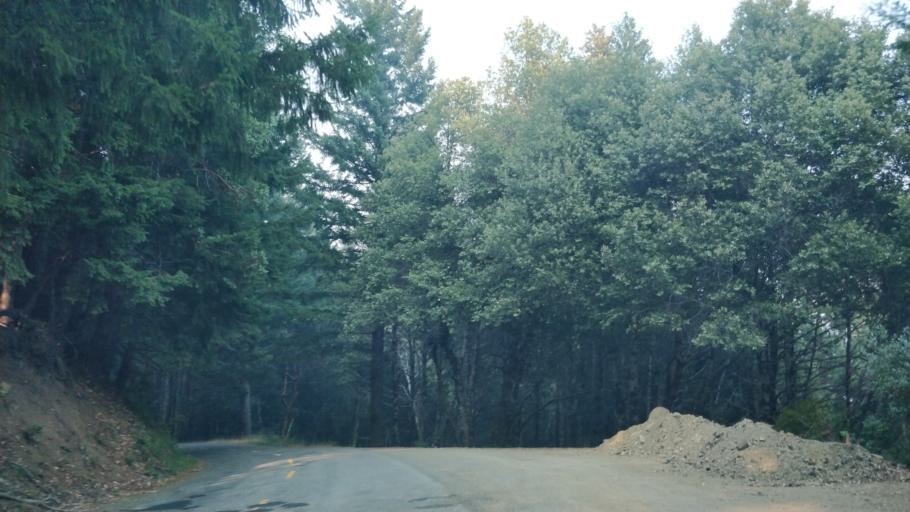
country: US
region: California
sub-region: Humboldt County
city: Rio Dell
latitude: 40.2976
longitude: -124.0566
